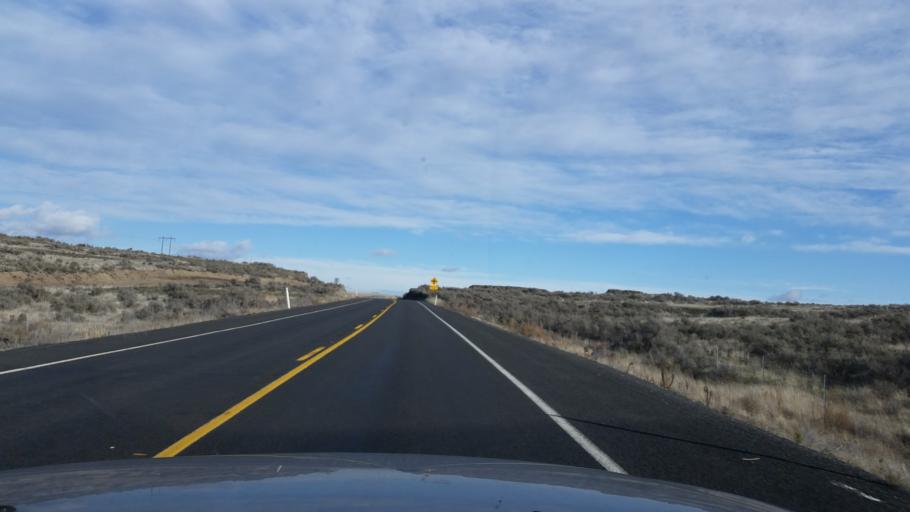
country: US
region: Washington
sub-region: Adams County
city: Ritzville
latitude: 47.3417
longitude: -118.6112
